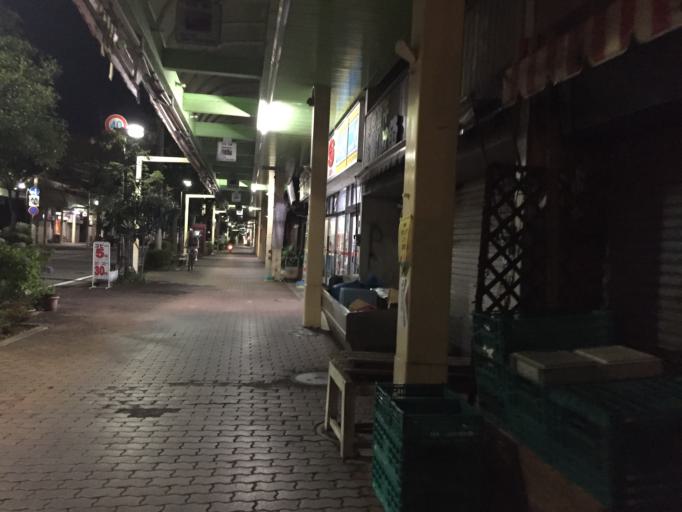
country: JP
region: Mie
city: Yokkaichi
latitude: 34.9650
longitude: 136.6312
